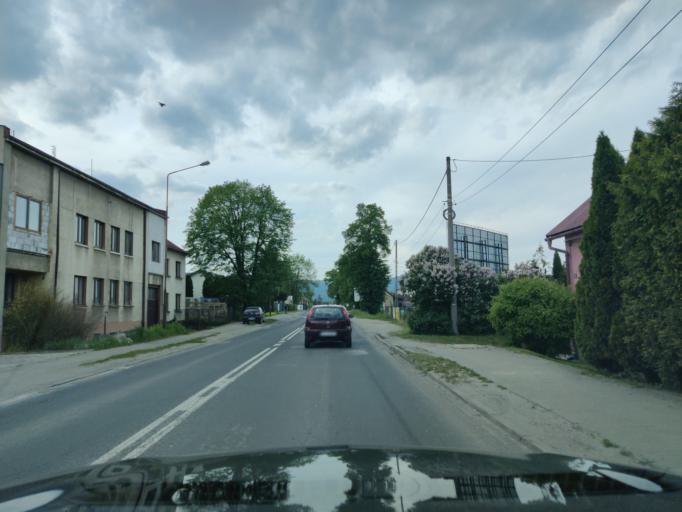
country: PL
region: Silesian Voivodeship
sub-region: Powiat zywiecki
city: Zywiec
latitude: 49.6871
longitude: 19.1836
